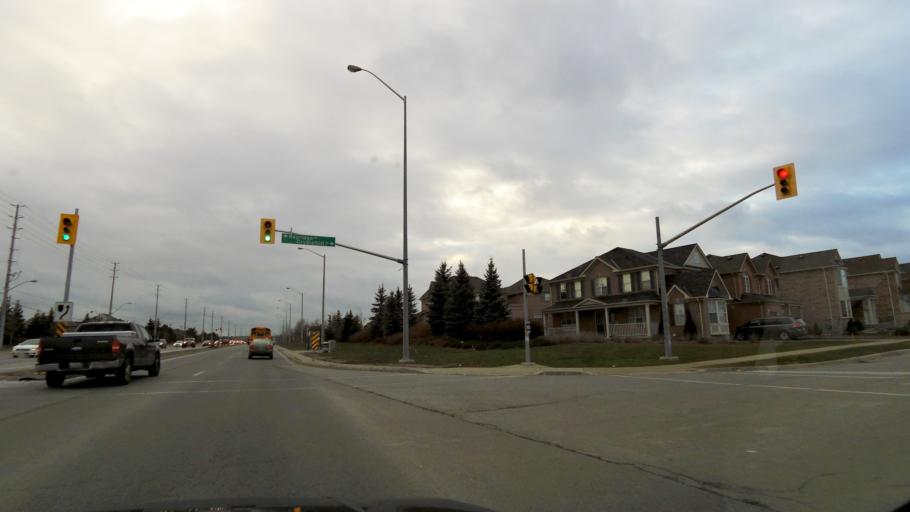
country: CA
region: Ontario
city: Brampton
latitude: 43.7697
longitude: -79.7149
